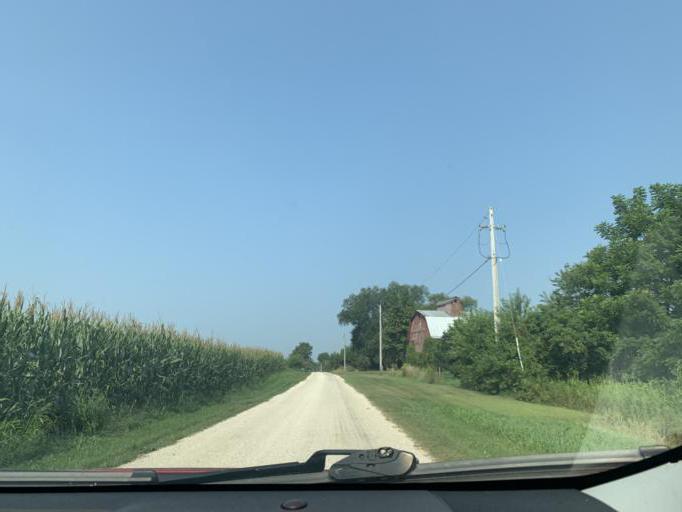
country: US
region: Illinois
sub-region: Whiteside County
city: Morrison
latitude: 41.8611
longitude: -89.8767
